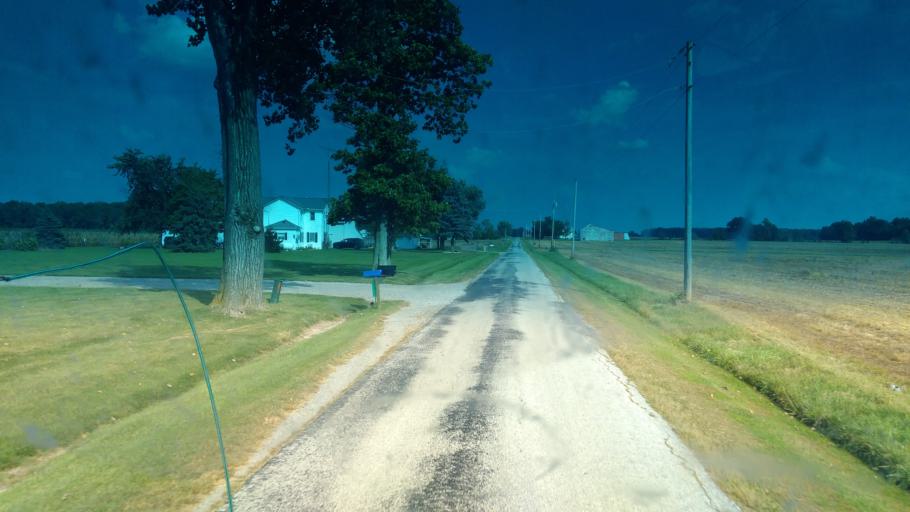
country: US
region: Ohio
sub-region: Hardin County
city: Forest
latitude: 40.8190
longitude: -83.5922
